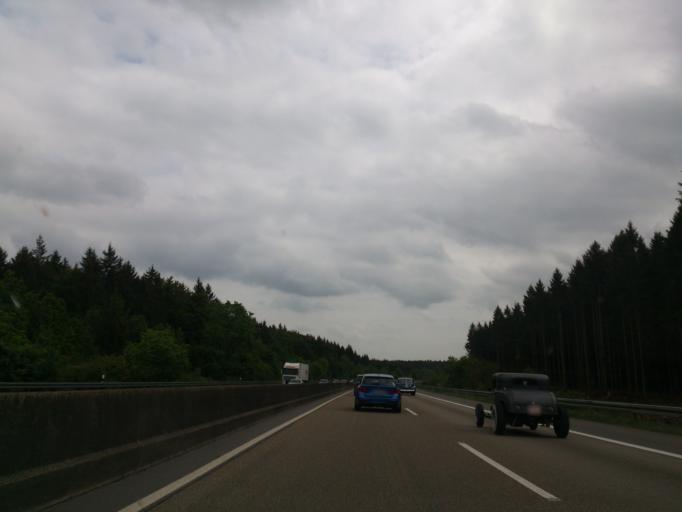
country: DE
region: Hesse
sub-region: Regierungsbezirk Kassel
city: Volkmarsen
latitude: 51.4398
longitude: 9.1484
